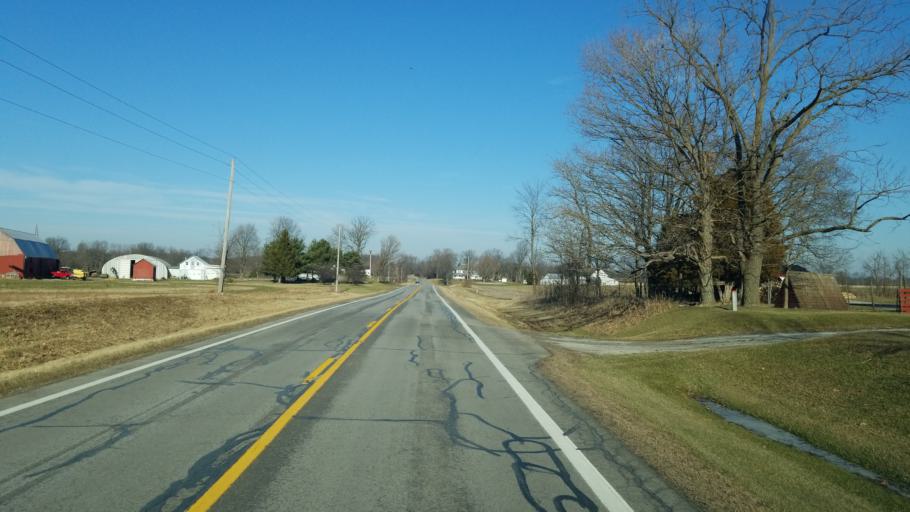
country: US
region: Ohio
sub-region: Huron County
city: Willard
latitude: 41.1324
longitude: -82.6590
